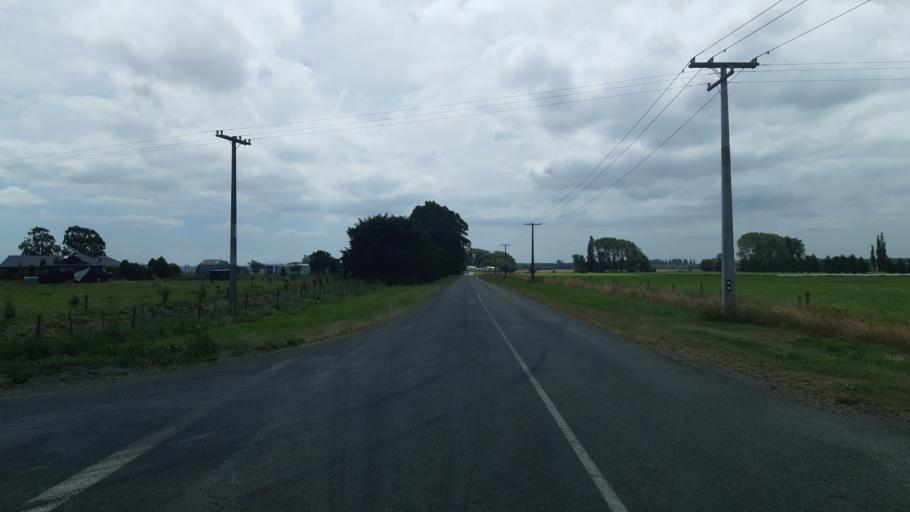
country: NZ
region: Canterbury
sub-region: Timaru District
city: Timaru
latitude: -44.2391
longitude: 171.3456
